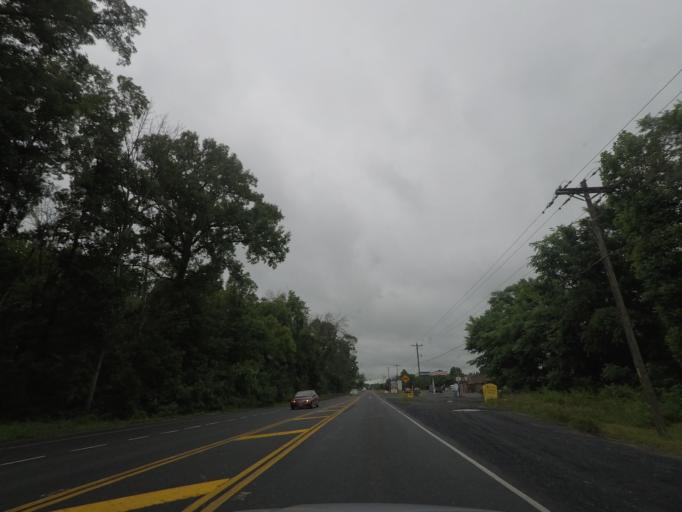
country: US
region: Virginia
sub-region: Prince William County
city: Bull Run Mountain Estates
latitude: 38.8787
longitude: -77.6340
